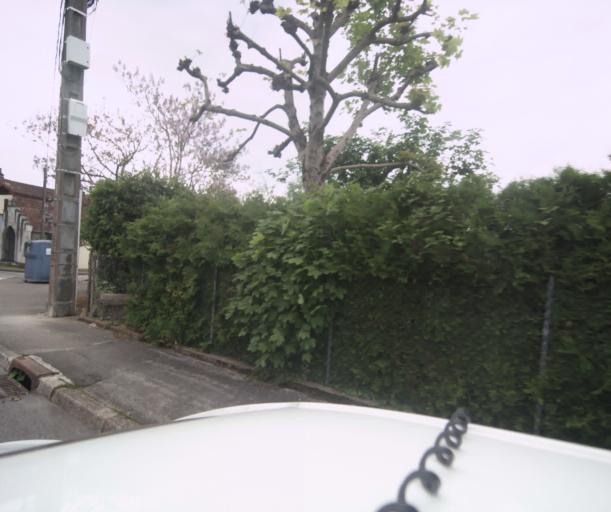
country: FR
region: Franche-Comte
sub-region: Departement du Doubs
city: Beure
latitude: 47.2302
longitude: 5.9853
